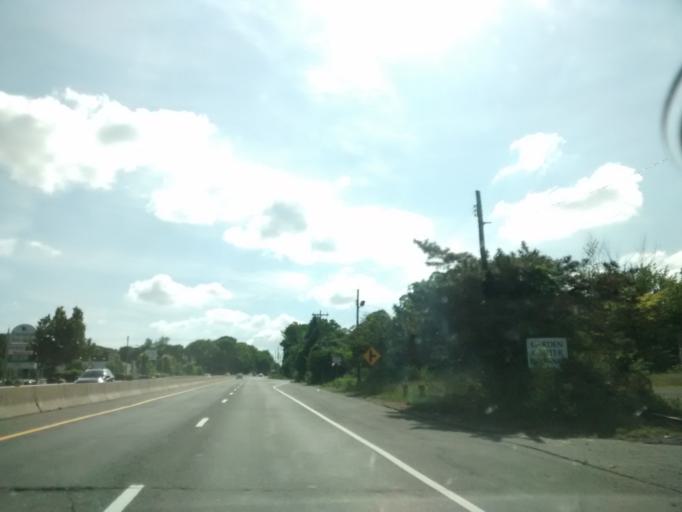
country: US
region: Massachusetts
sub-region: Worcester County
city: Shrewsbury
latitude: 42.2809
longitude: -71.6758
